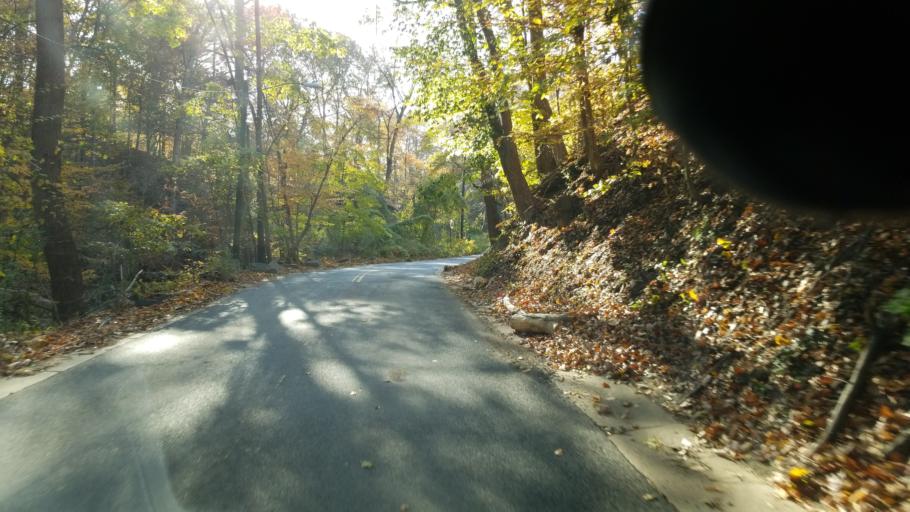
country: US
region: Maryland
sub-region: Montgomery County
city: Chevy Chase
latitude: 38.9531
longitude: -77.0553
